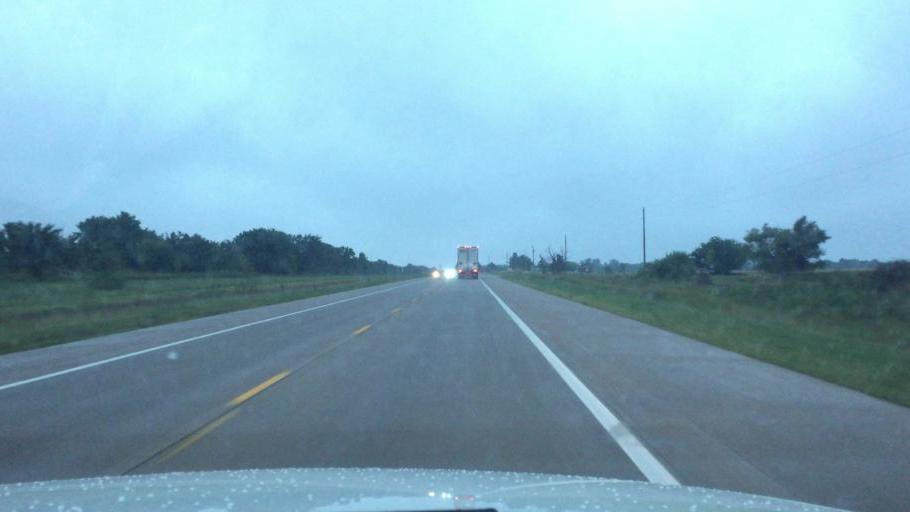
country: US
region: Kansas
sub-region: Neosho County
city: Chanute
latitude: 37.5067
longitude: -95.4709
